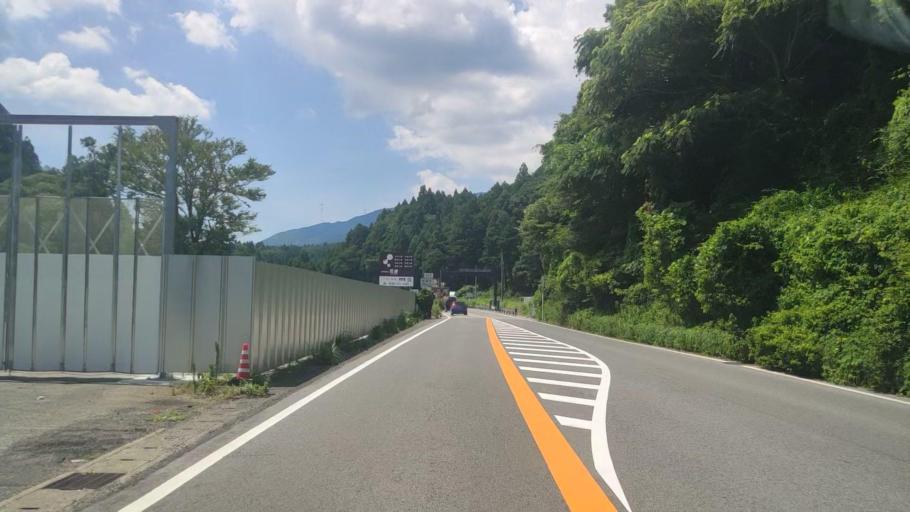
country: JP
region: Gifu
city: Tarui
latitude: 35.3795
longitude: 136.4376
